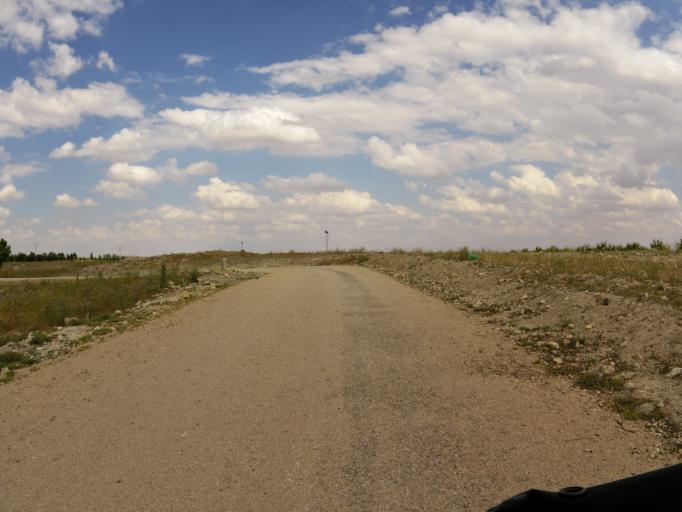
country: ES
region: Castille-La Mancha
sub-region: Provincia de Albacete
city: Albacete
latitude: 38.9583
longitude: -1.9737
